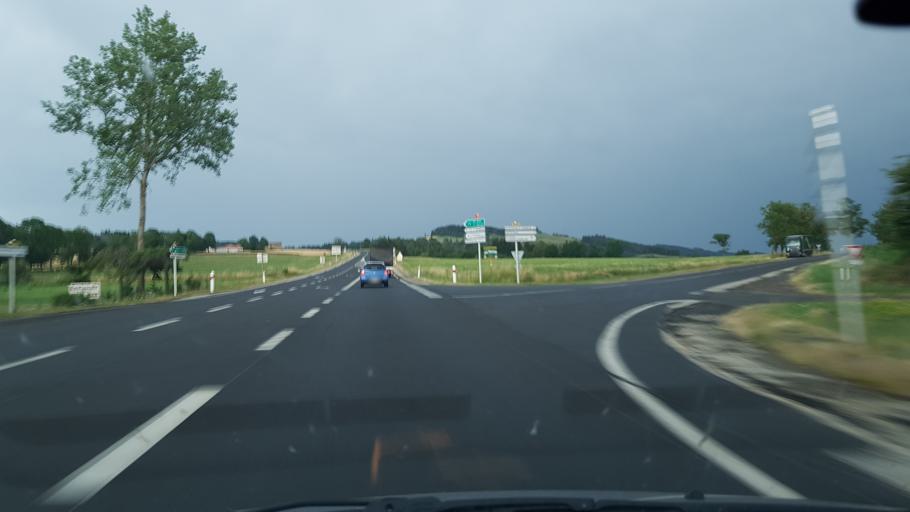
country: FR
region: Auvergne
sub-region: Departement de la Haute-Loire
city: Allegre
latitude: 45.1384
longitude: 3.6313
